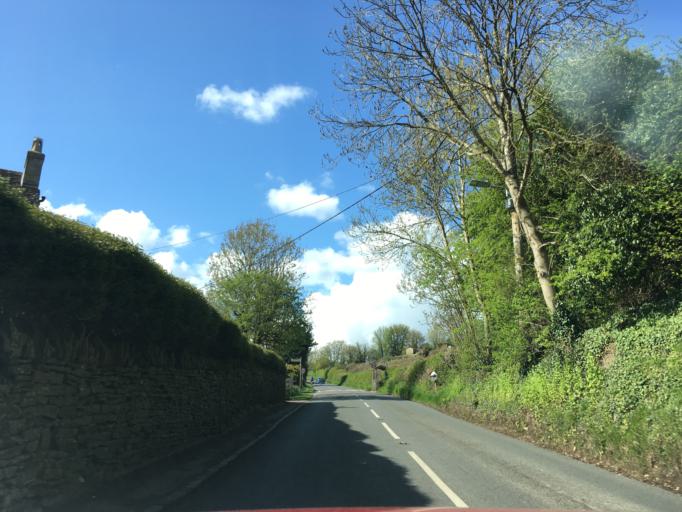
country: GB
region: England
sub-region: Gloucestershire
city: Minchinhampton
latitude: 51.6812
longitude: -2.1652
